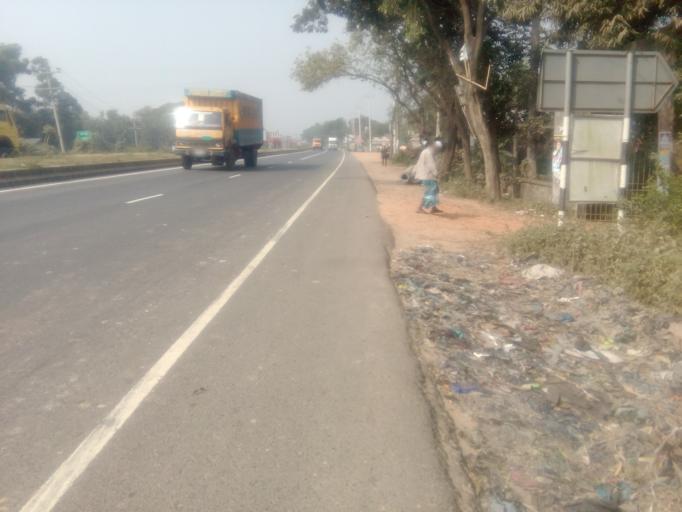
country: IN
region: Tripura
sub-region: West Tripura
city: Sonamura
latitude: 23.3209
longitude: 91.2816
